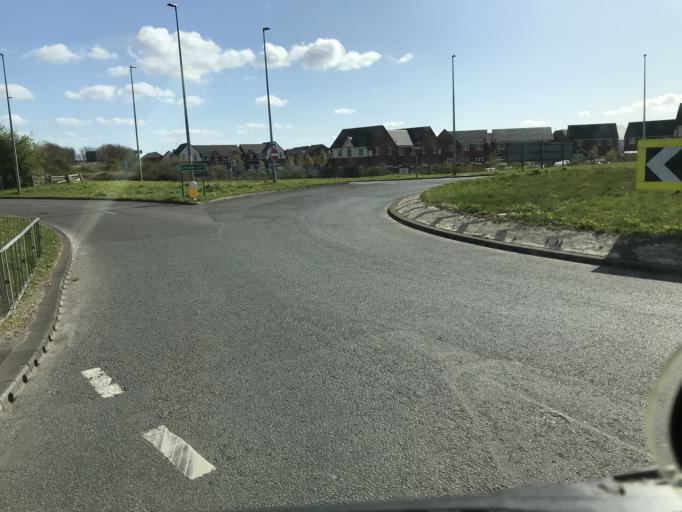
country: GB
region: Wales
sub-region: County of Flintshire
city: Hawarden
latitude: 53.1668
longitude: -2.9783
